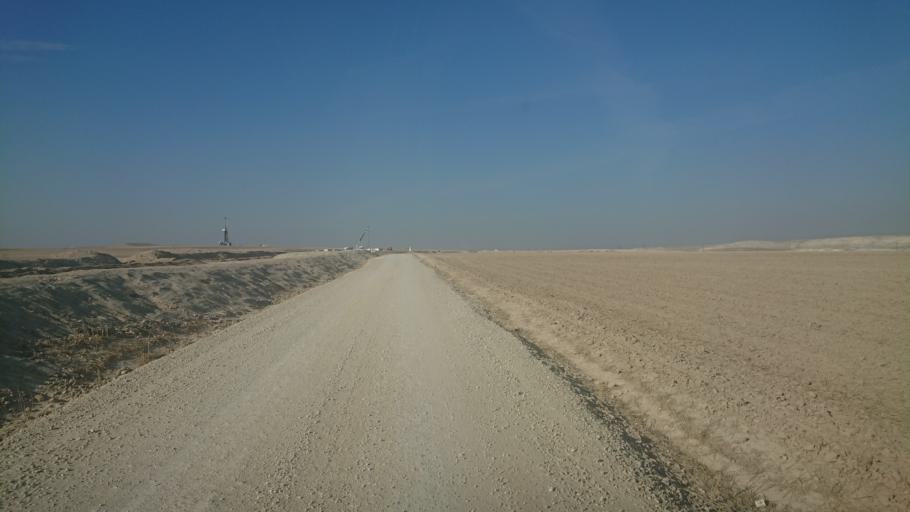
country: TR
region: Aksaray
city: Sultanhani
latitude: 38.0697
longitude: 33.6145
